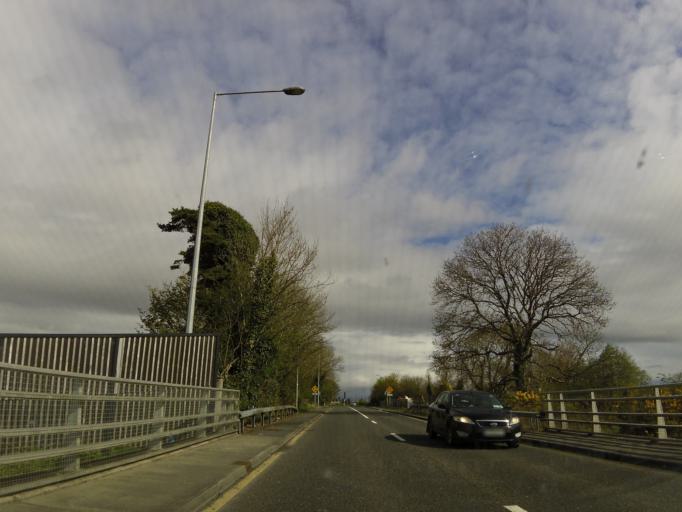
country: IE
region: Connaught
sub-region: Sligo
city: Tobercurry
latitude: 53.9535
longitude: -8.7931
